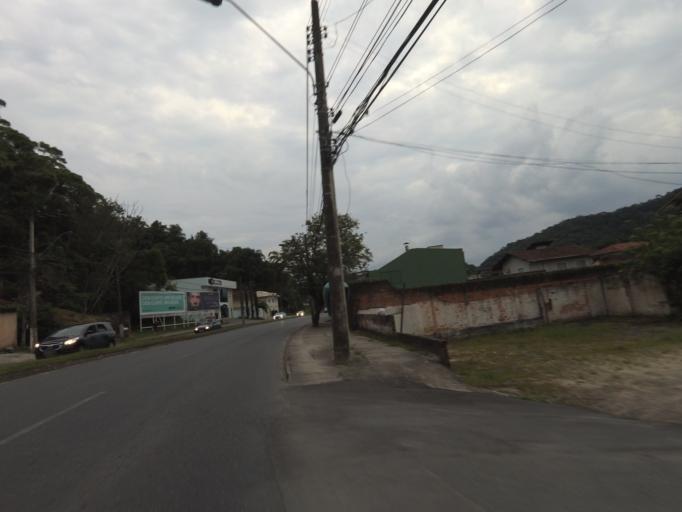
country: BR
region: Santa Catarina
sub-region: Blumenau
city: Blumenau
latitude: -26.9029
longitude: -49.0630
